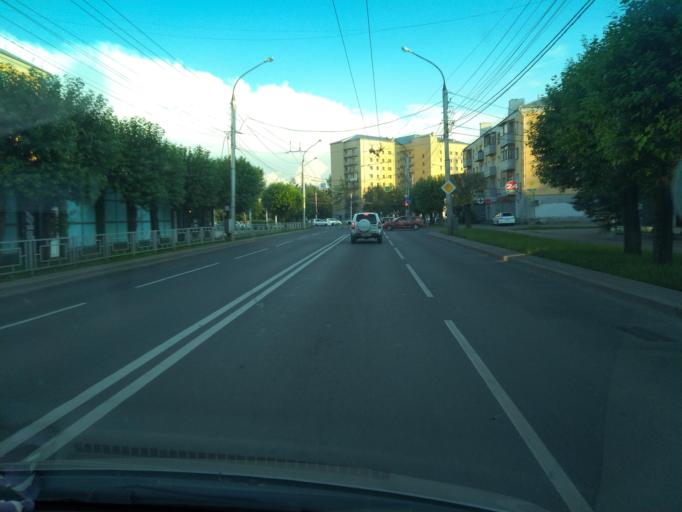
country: RU
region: Krasnoyarskiy
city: Krasnoyarsk
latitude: 56.0275
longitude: 92.9074
